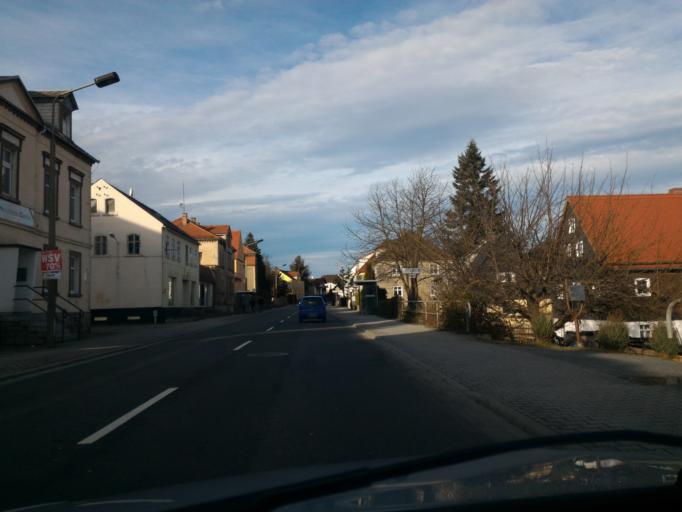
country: DE
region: Saxony
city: Neukirch/Lausitz
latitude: 51.0949
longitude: 14.3117
